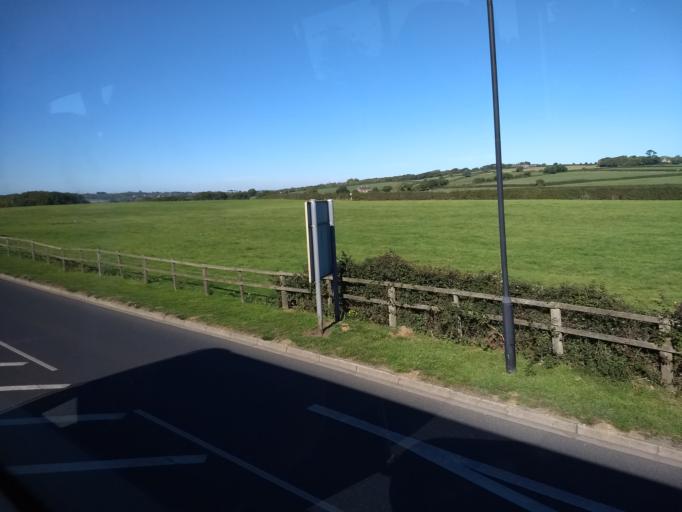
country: GB
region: England
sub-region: Isle of Wight
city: Newport
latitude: 50.7247
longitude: -1.2559
